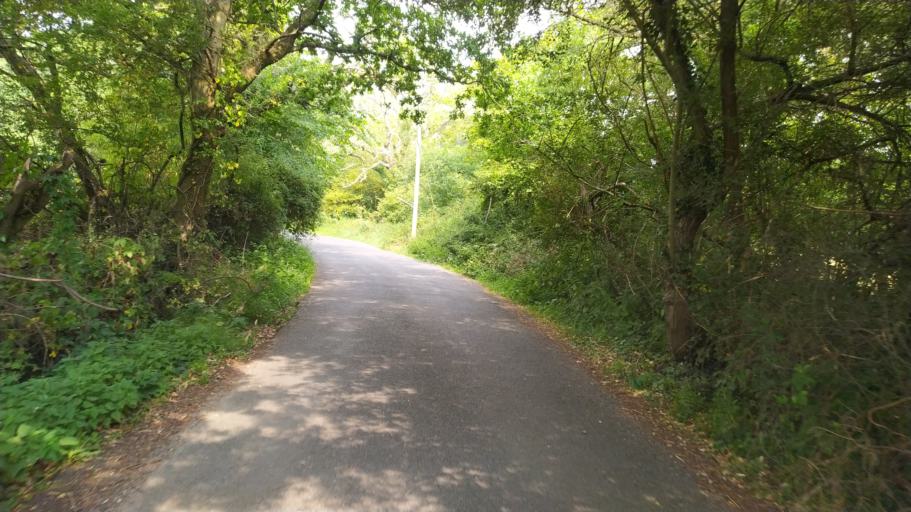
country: GB
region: England
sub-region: Hampshire
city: Romsey
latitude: 50.9957
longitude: -1.4499
